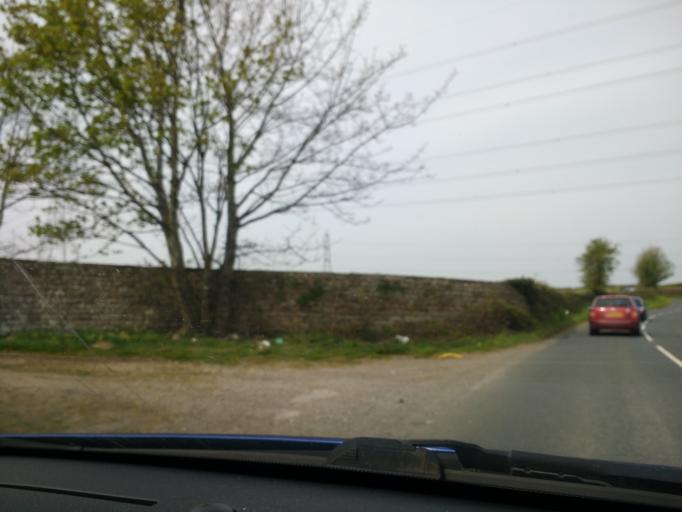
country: GB
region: England
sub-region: Lancashire
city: Lancaster
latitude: 54.0157
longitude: -2.8126
